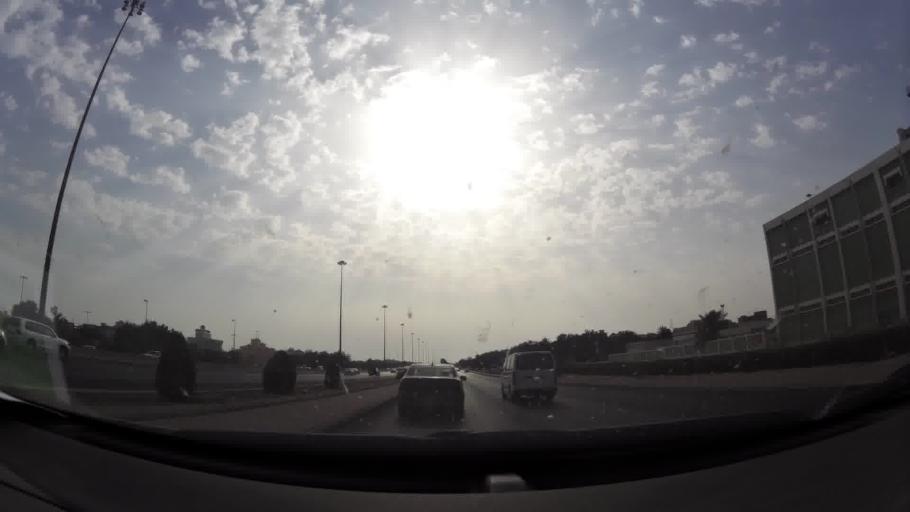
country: KW
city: Bayan
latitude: 29.3102
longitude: 48.0556
